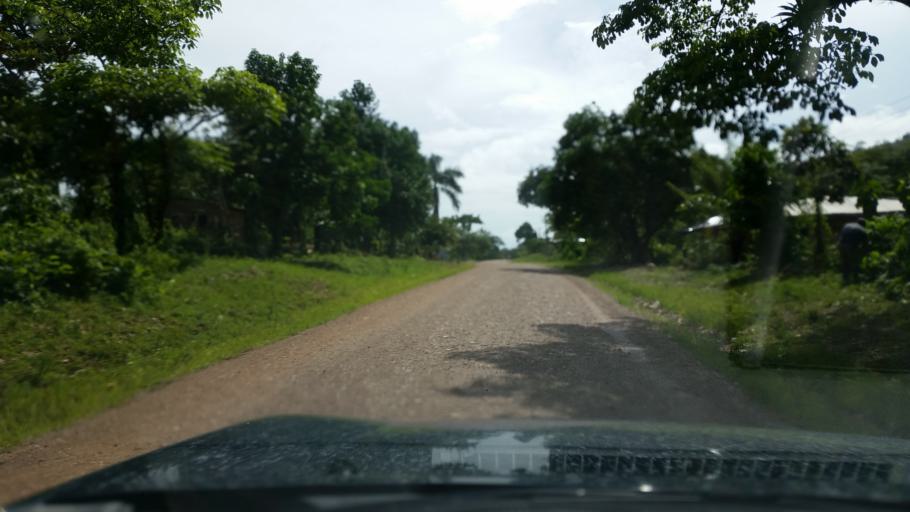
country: NI
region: Atlantico Norte (RAAN)
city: Siuna
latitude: 13.6815
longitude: -84.6462
